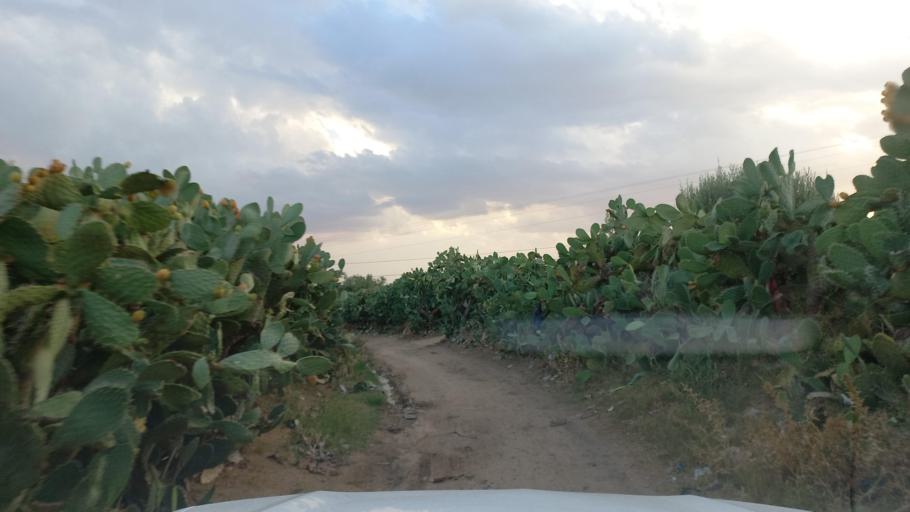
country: TN
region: Al Qasrayn
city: Kasserine
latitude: 35.2712
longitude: 9.0666
